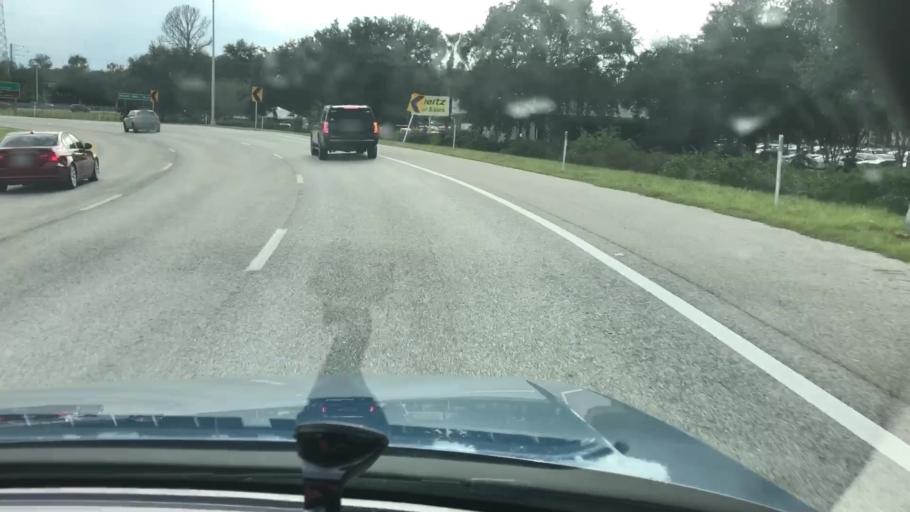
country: US
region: Florida
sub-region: Seminole County
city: Lake Mary
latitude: 28.8131
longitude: -81.3396
